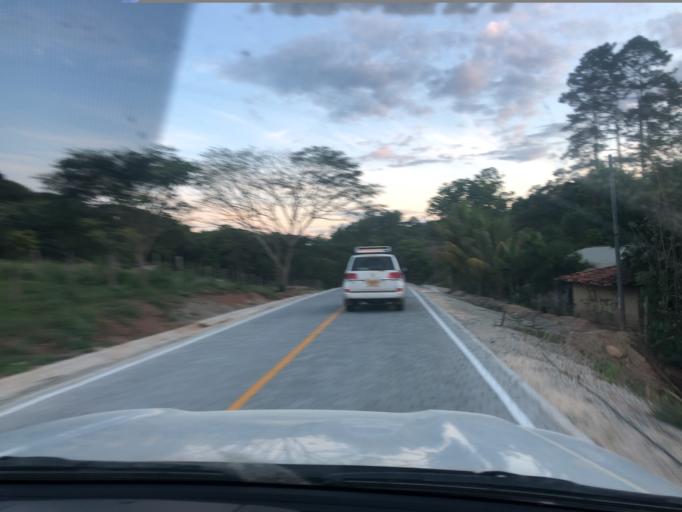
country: NI
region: Nueva Segovia
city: Ocotal
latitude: 13.6792
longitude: -86.6203
